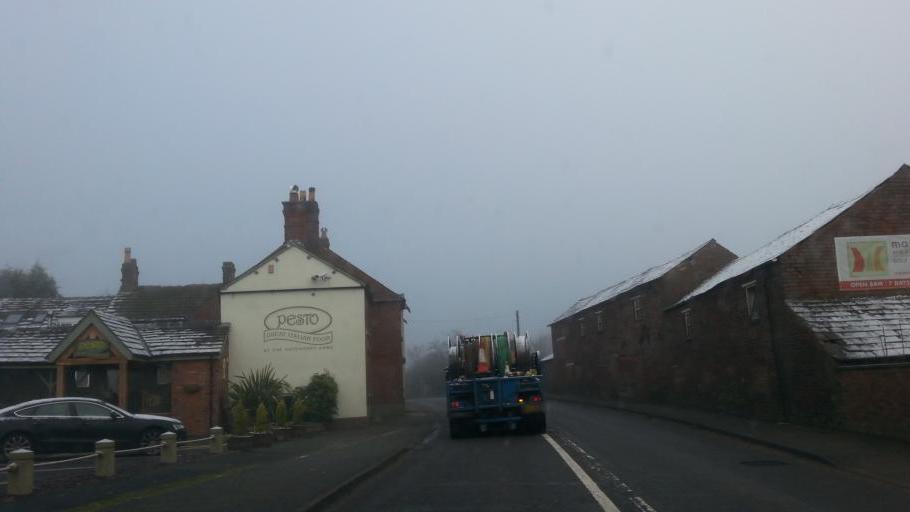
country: GB
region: England
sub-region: Cheshire East
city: Siddington
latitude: 53.2096
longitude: -2.2260
